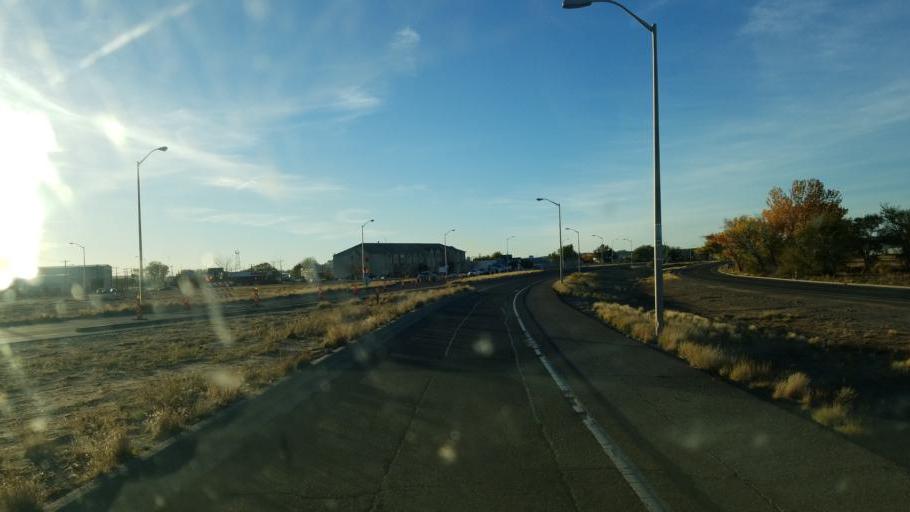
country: US
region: New Mexico
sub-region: San Juan County
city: Farmington
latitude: 36.7199
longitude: -108.1825
